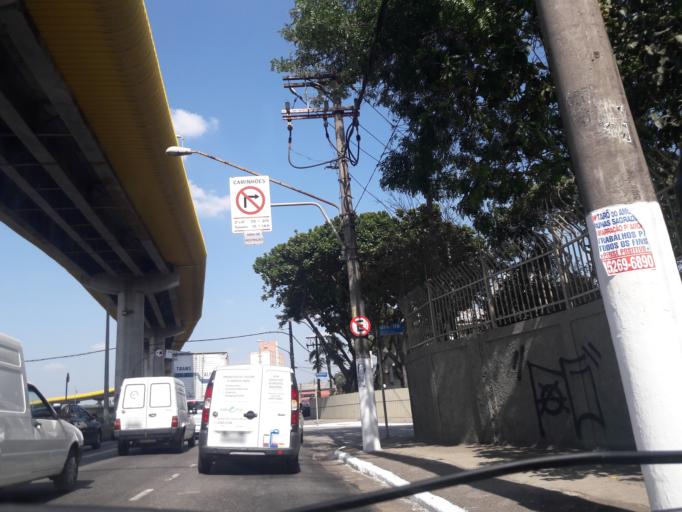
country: BR
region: Sao Paulo
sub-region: Sao Paulo
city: Sao Paulo
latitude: -23.5850
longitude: -46.5996
